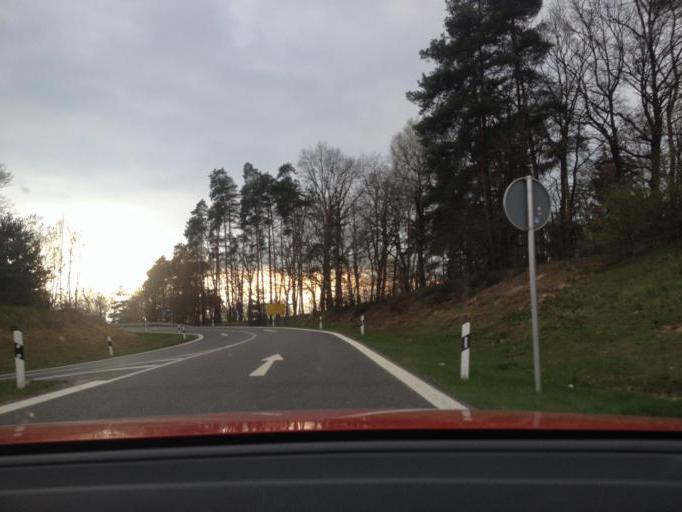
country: DE
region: Bavaria
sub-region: Regierungsbezirk Mittelfranken
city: Neunkirchen am Sand
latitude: 49.5184
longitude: 11.3056
